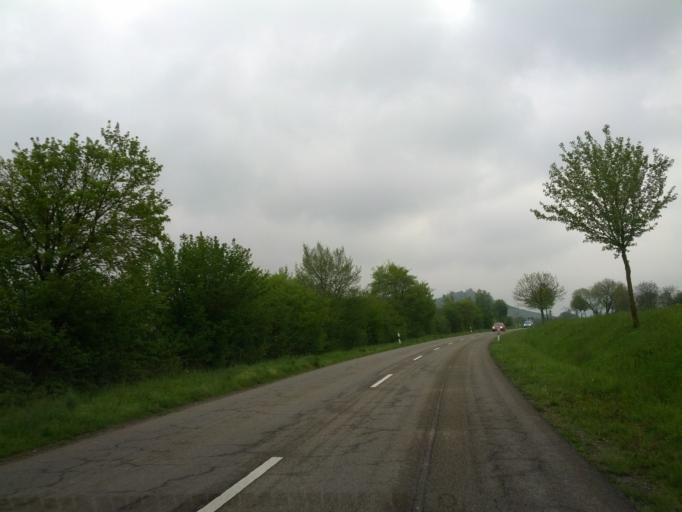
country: DE
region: Baden-Wuerttemberg
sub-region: Freiburg Region
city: Pfaffenweiler
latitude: 47.8995
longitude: 7.7370
